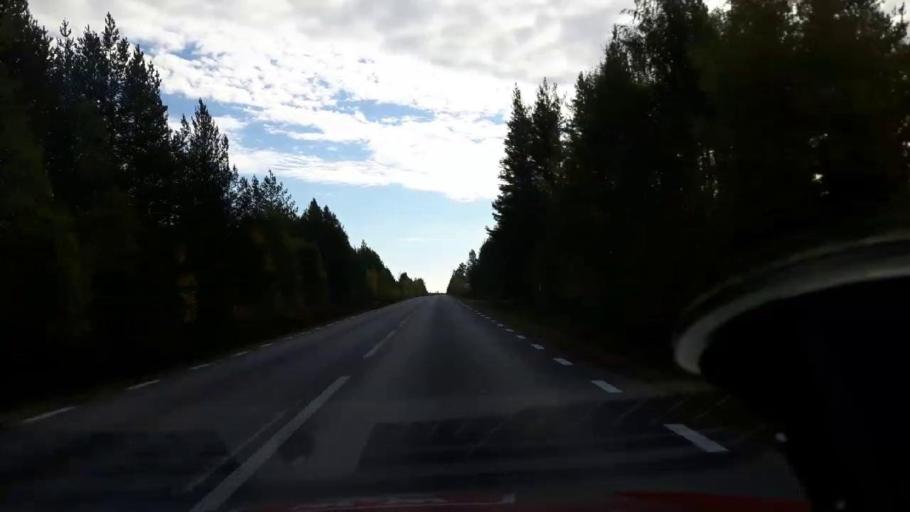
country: SE
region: Gaevleborg
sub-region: Ljusdals Kommun
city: Farila
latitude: 61.9911
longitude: 15.2653
